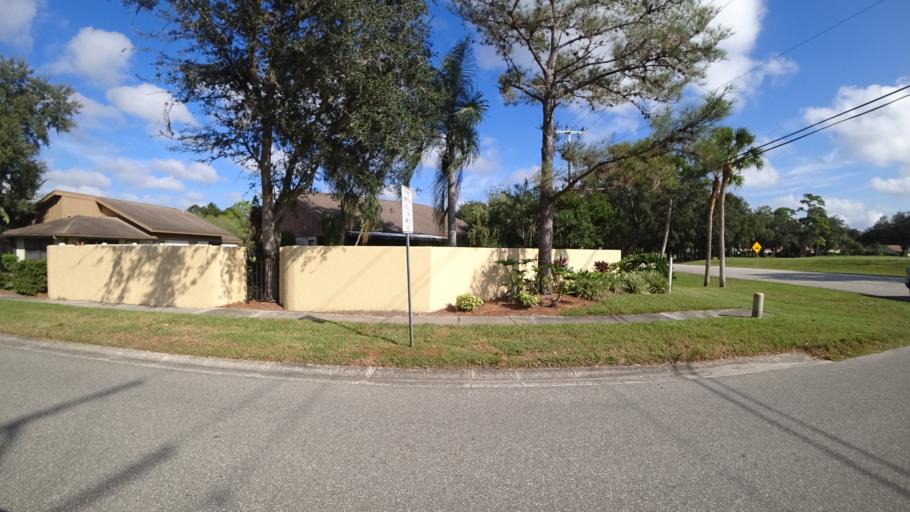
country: US
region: Florida
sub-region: Sarasota County
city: Desoto Lakes
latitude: 27.3994
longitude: -82.4874
